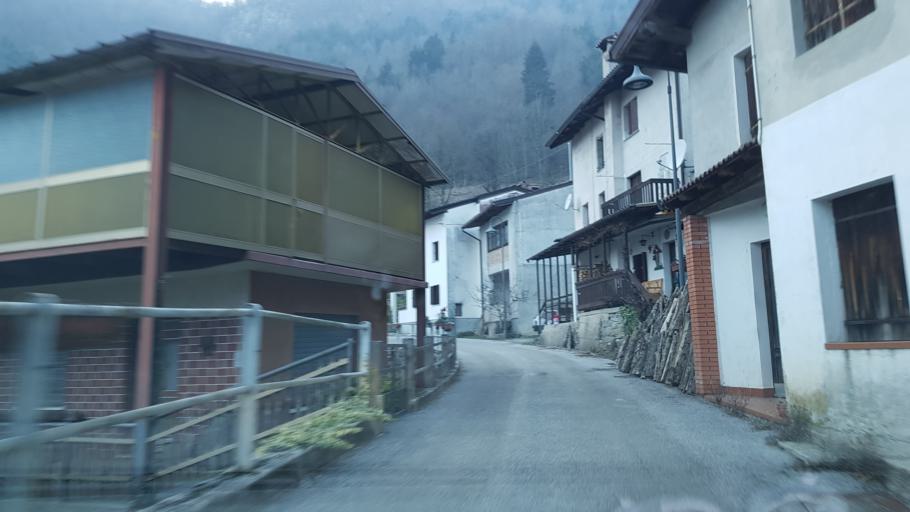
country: IT
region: Friuli Venezia Giulia
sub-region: Provincia di Udine
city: Taipana
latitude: 46.2260
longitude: 13.4020
